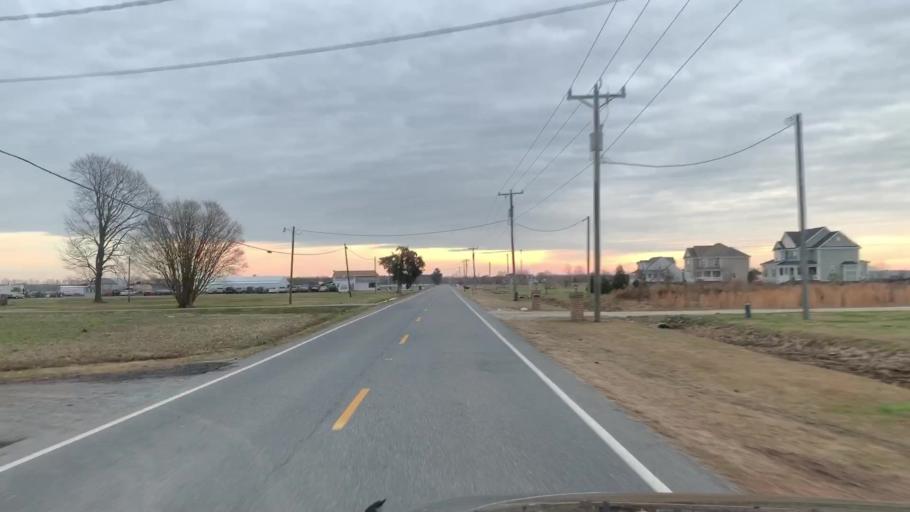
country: US
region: North Carolina
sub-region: Currituck County
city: Moyock
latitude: 36.6236
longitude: -76.1567
